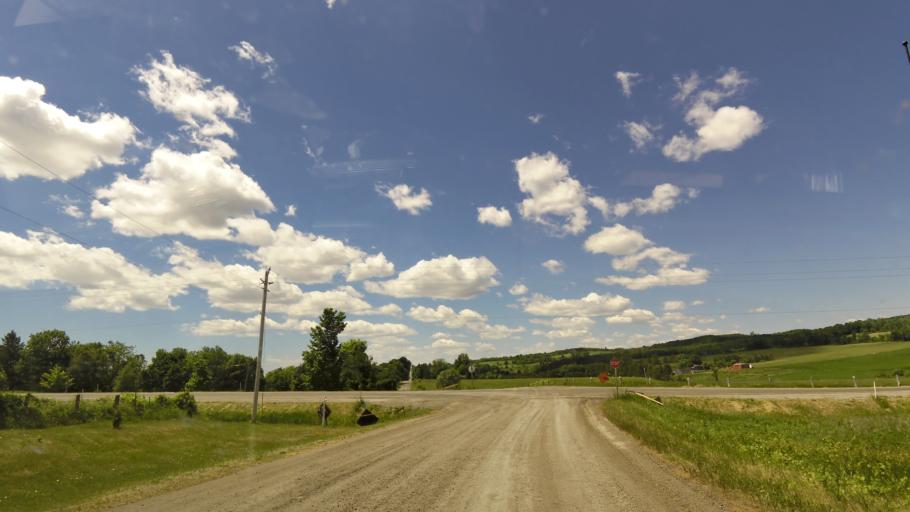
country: CA
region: Ontario
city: Omemee
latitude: 43.9937
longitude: -78.5151
